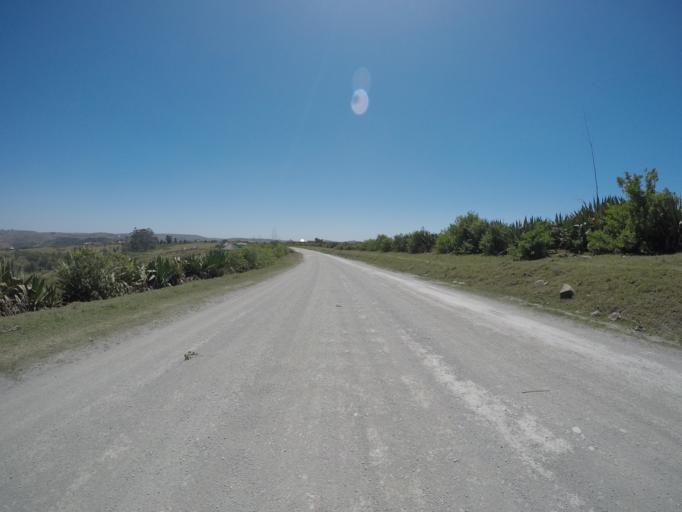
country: ZA
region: Eastern Cape
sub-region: OR Tambo District Municipality
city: Libode
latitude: -32.0084
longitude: 29.0736
